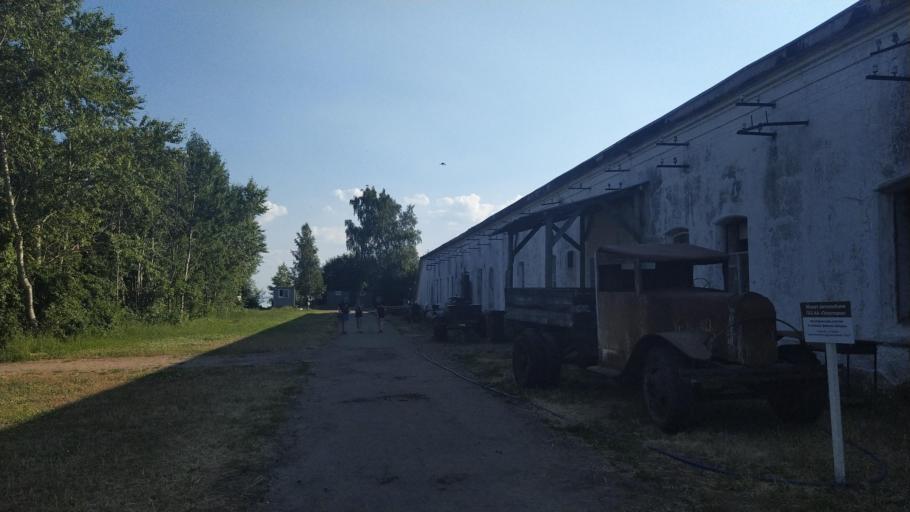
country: RU
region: St.-Petersburg
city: Bol'shaya Izhora
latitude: 60.0324
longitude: 29.6390
